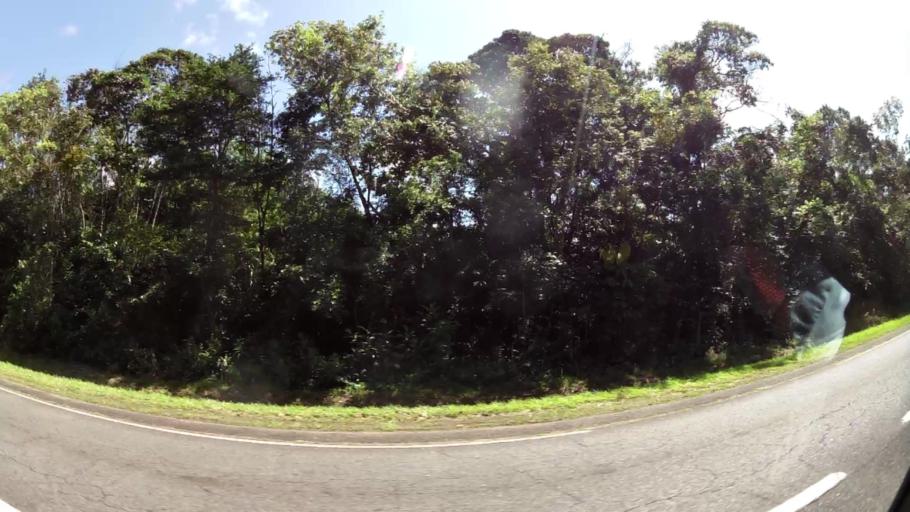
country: GF
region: Guyane
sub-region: Guyane
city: Matoury
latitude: 4.8369
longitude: -52.3362
